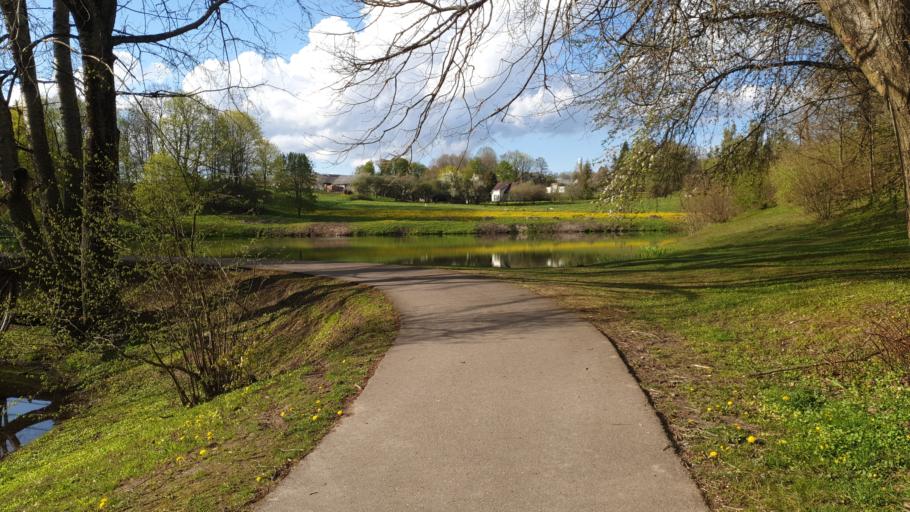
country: LT
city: Gelgaudiskis
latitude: 55.0986
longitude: 22.9886
